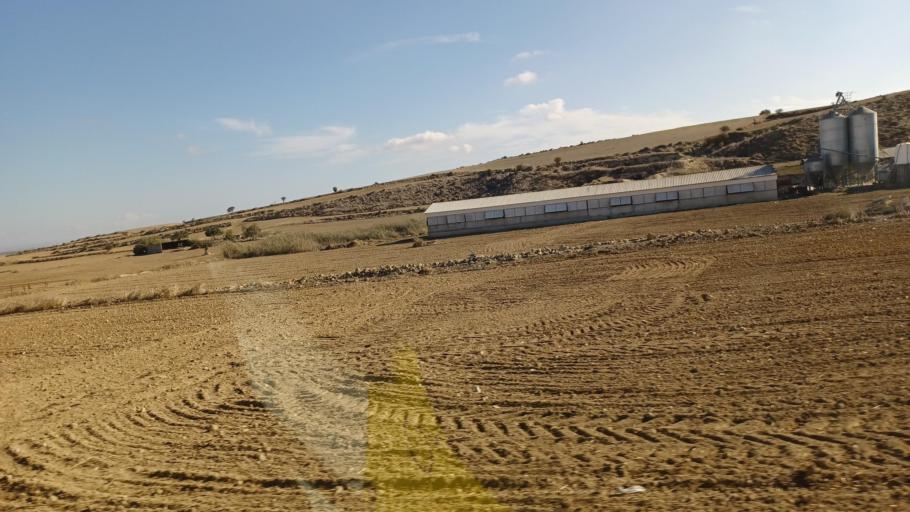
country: CY
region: Larnaka
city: Athienou
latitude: 35.0441
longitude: 33.5554
